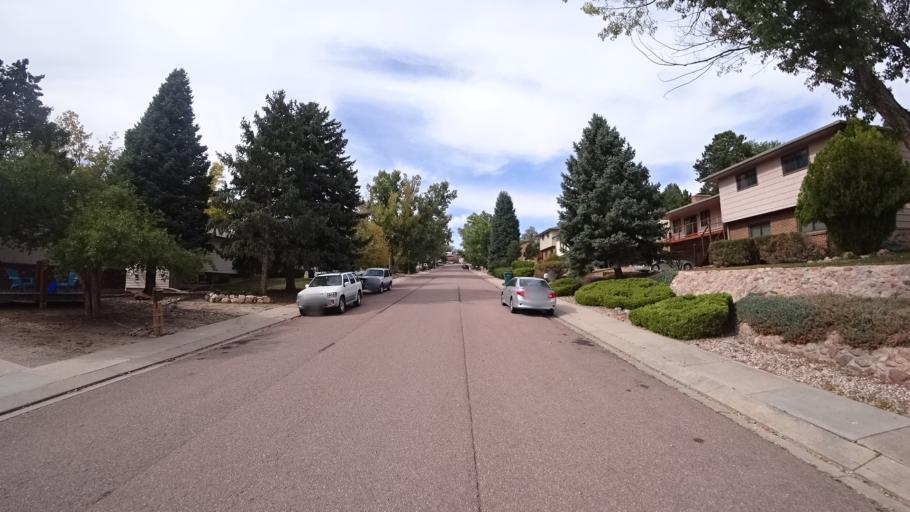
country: US
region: Colorado
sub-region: El Paso County
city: Colorado Springs
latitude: 38.9014
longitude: -104.7830
